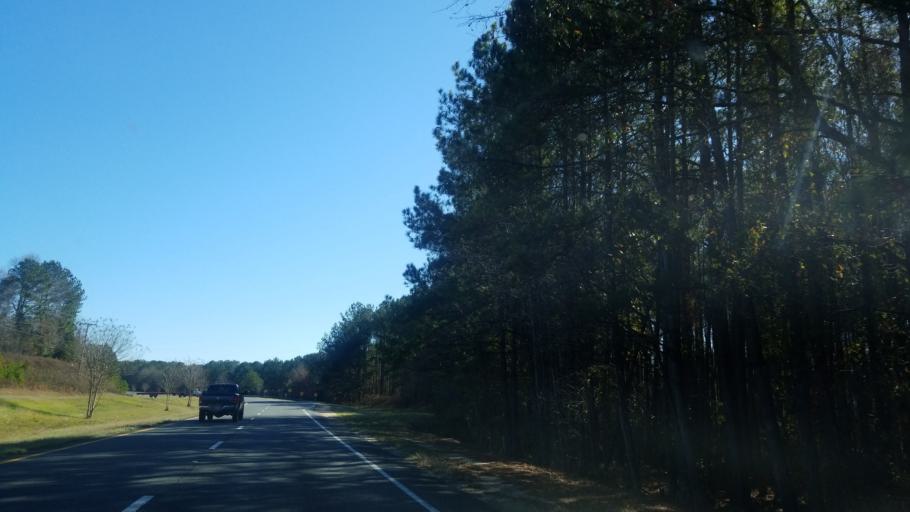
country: US
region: Georgia
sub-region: Talbot County
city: Talbotton
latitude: 32.5473
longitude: -84.7288
